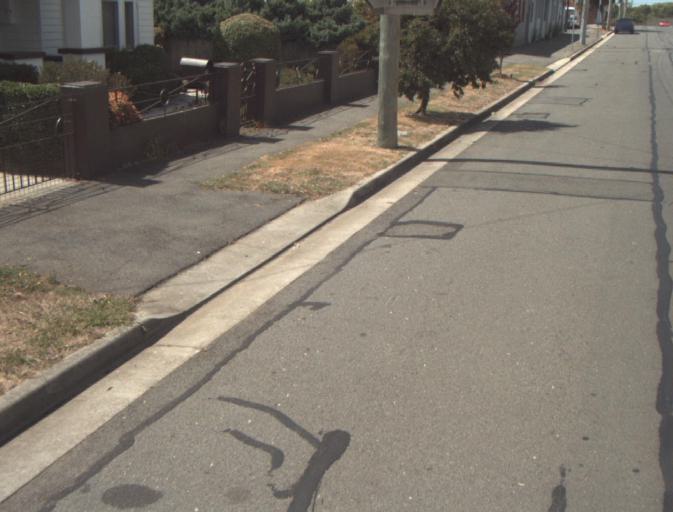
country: AU
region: Tasmania
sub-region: Launceston
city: Launceston
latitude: -41.4196
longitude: 147.1403
